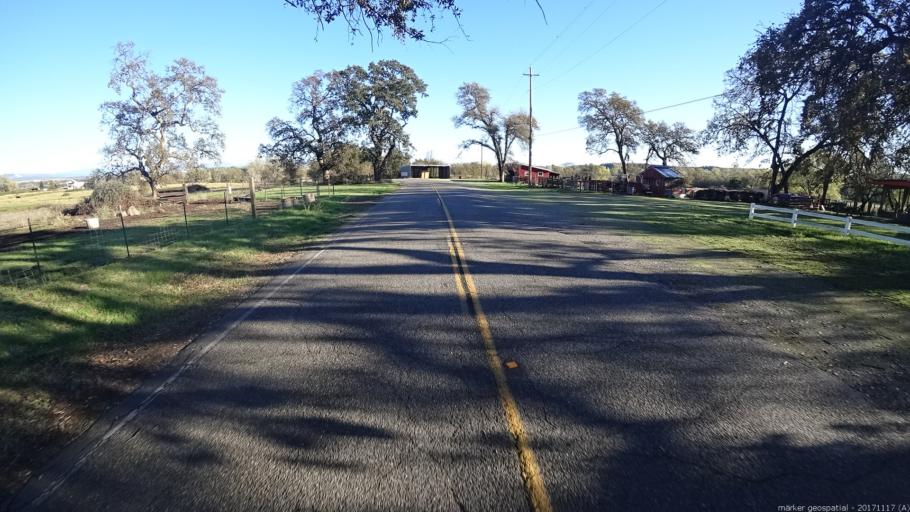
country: US
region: California
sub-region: Shasta County
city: Cottonwood
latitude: 40.3925
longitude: -122.2134
